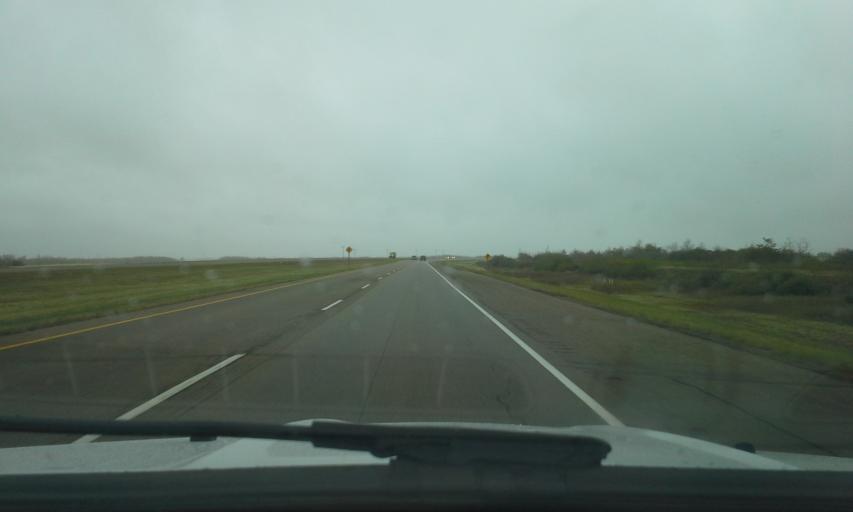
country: CA
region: Saskatchewan
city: Lloydminster
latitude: 53.2288
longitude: -109.8304
